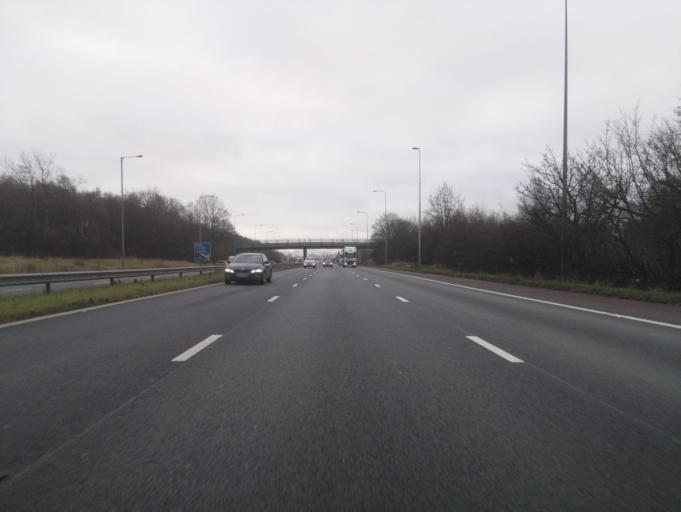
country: GB
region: England
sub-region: Lancashire
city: Coppull
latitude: 53.6092
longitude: -2.6880
